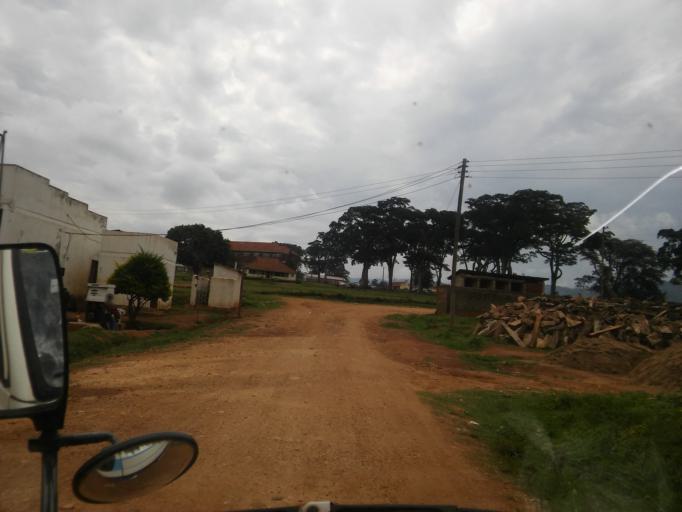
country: UG
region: Eastern Region
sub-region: Bududa District
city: Bududa
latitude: 0.9492
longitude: 34.2743
